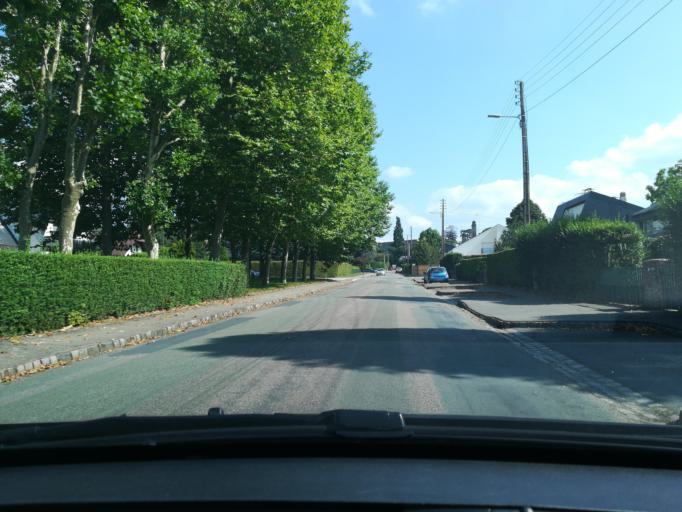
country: FR
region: Haute-Normandie
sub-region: Departement de la Seine-Maritime
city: Bois-Guillaume
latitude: 49.4669
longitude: 1.1110
